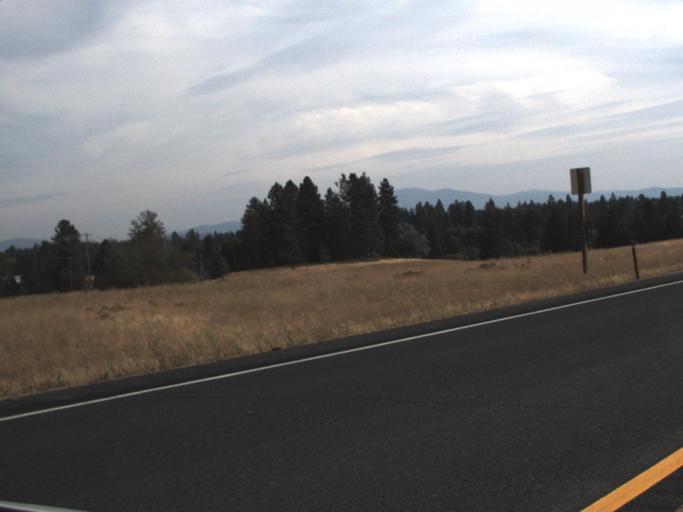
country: US
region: Washington
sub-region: Spokane County
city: Deer Park
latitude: 47.9600
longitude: -117.4956
